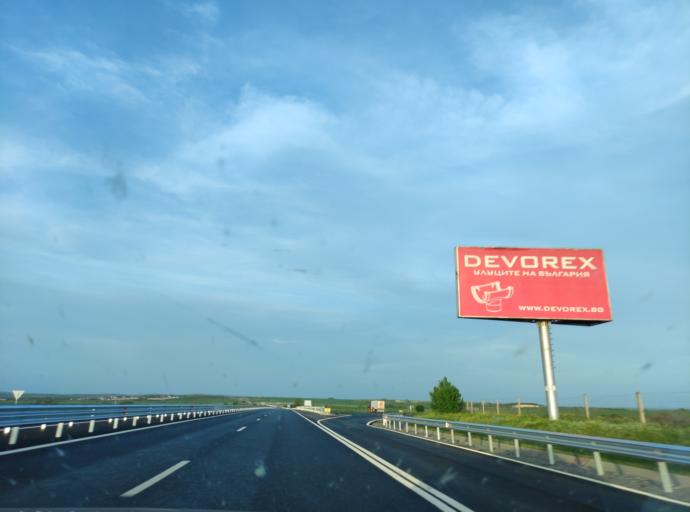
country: BG
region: Stara Zagora
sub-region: Obshtina Chirpan
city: Chirpan
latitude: 42.1953
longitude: 25.2480
